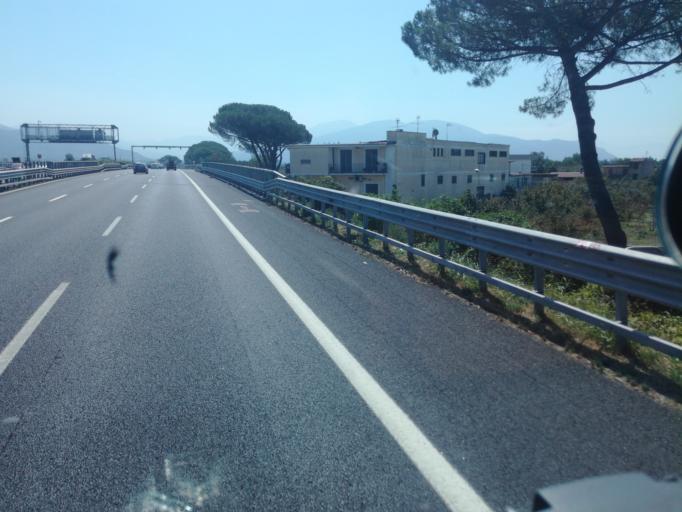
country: IT
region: Campania
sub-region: Provincia di Napoli
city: Nola
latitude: 40.9173
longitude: 14.5165
